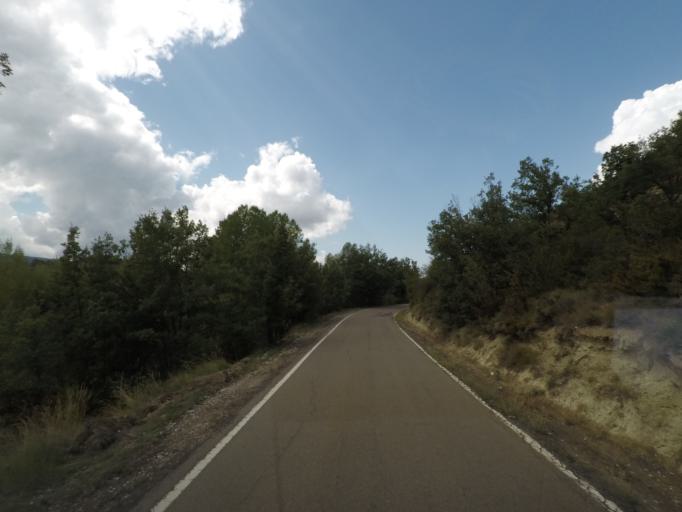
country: ES
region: Aragon
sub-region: Provincia de Huesca
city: Yebra de Basa
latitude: 42.3900
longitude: -0.2813
